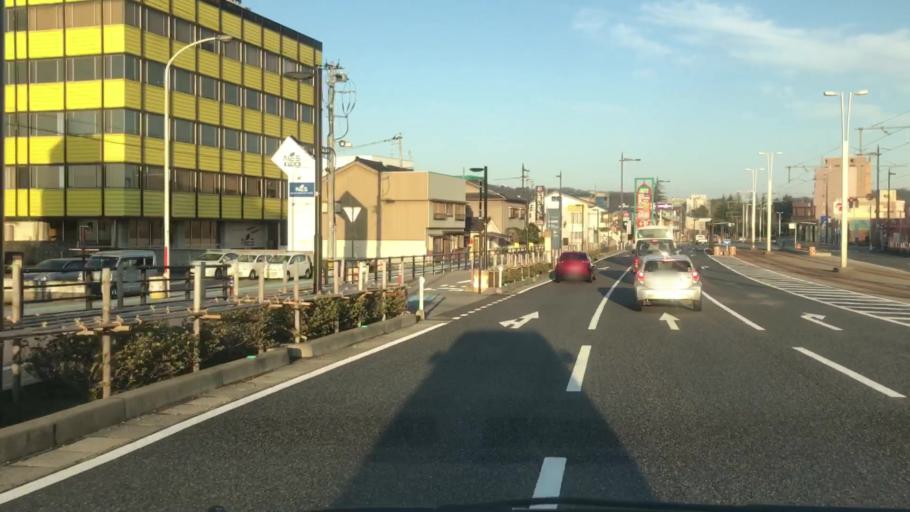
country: JP
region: Toyama
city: Toyama-shi
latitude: 36.6951
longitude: 137.1952
